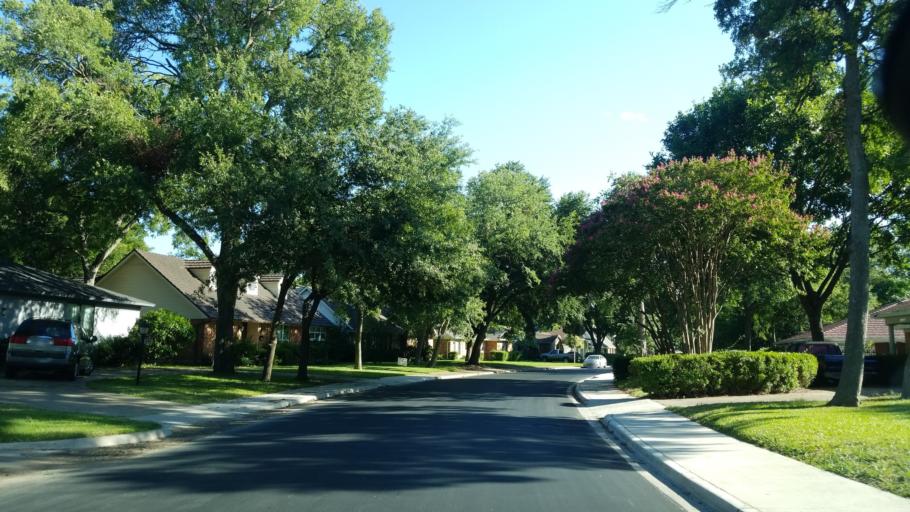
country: US
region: Texas
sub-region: Dallas County
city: Highland Park
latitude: 32.7895
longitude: -96.7050
